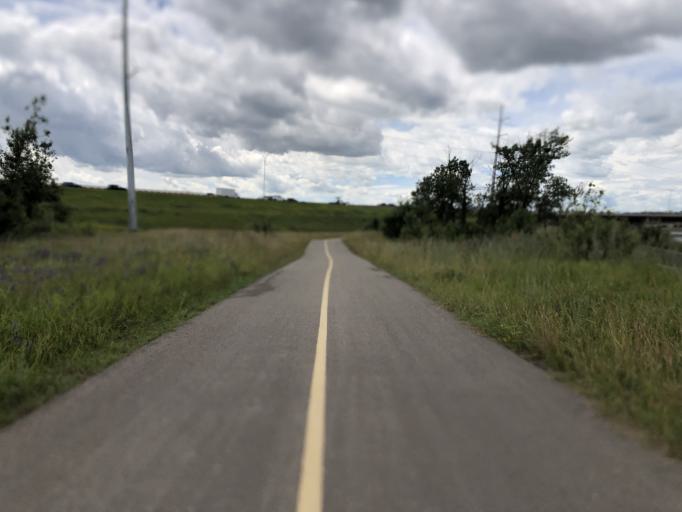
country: CA
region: Alberta
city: Calgary
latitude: 51.0101
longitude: -114.0144
